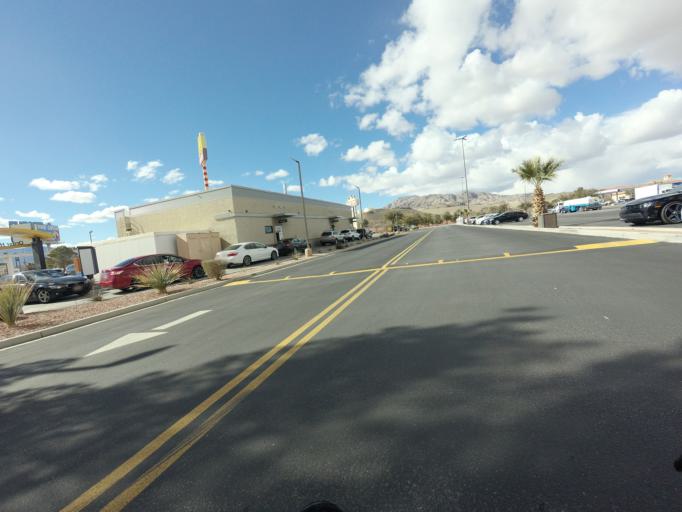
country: US
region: Nevada
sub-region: Clark County
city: Sandy Valley
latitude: 35.6101
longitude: -115.3876
